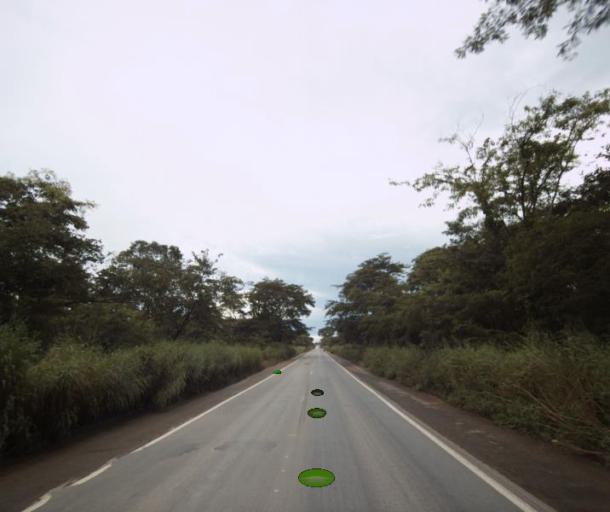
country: BR
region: Goias
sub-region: Porangatu
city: Porangatu
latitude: -13.5544
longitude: -49.0778
